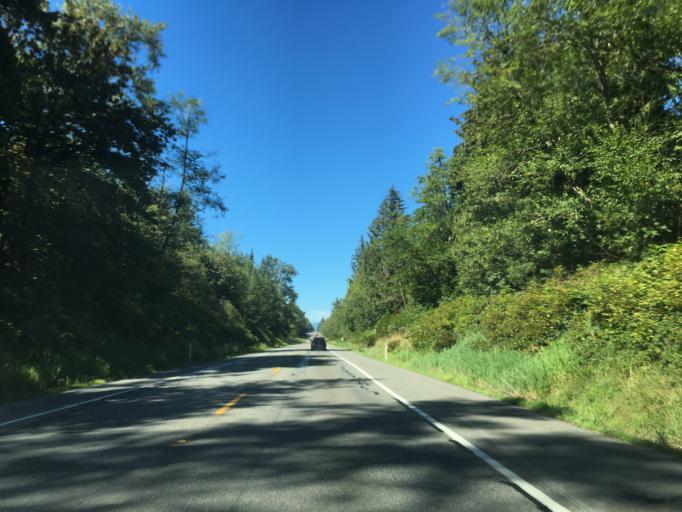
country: US
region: Washington
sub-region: Snohomish County
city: Sisco Heights
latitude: 48.0625
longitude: -122.1111
